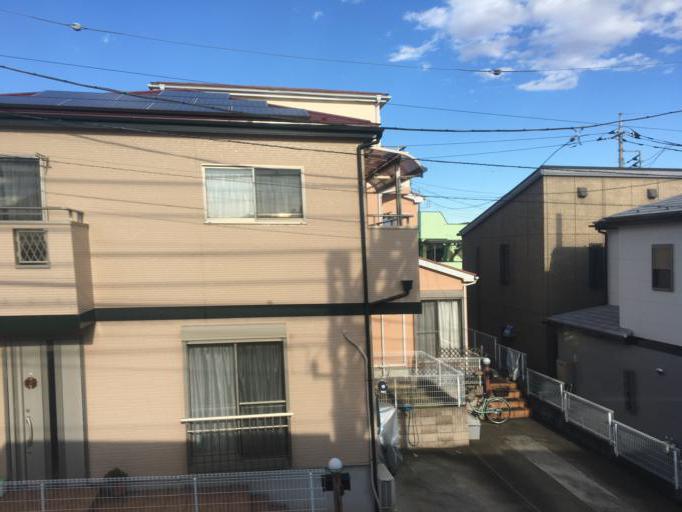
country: JP
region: Saitama
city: Oi
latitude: 35.8559
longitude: 139.5275
